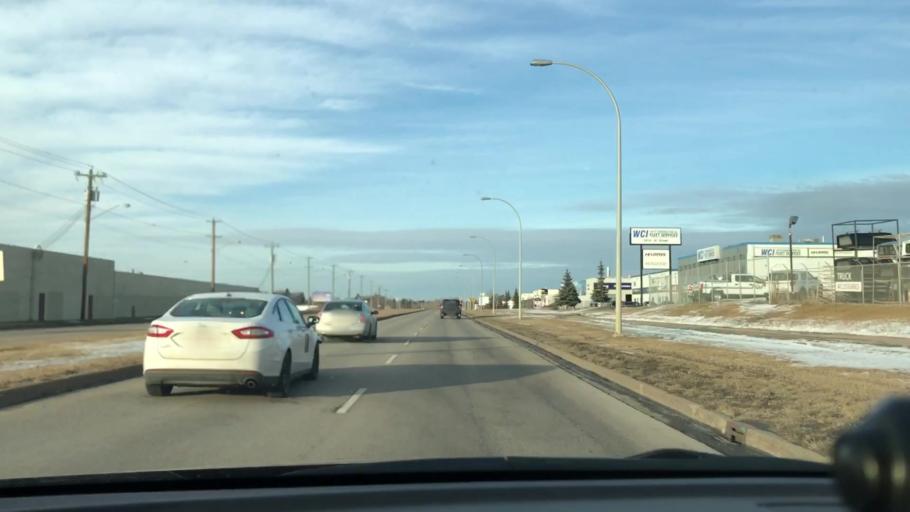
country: CA
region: Alberta
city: Edmonton
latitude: 53.4946
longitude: -113.4670
